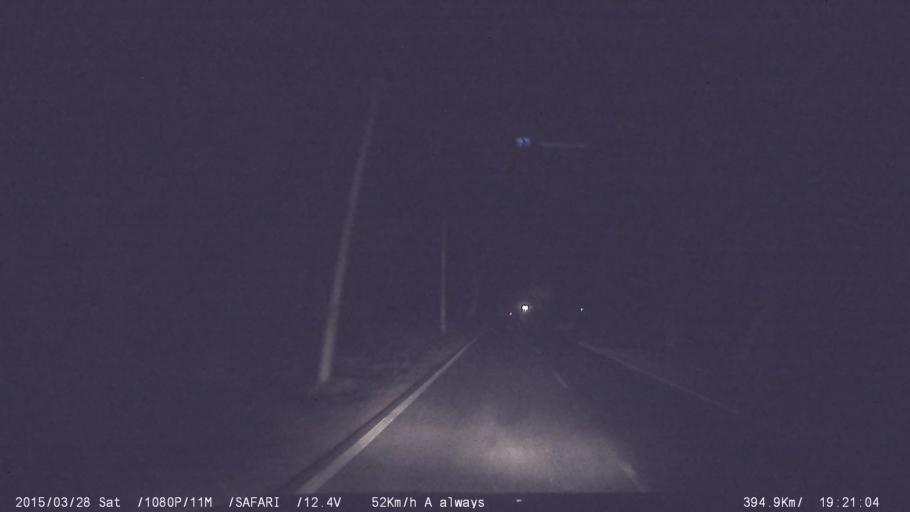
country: IN
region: Karnataka
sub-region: Mandya
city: Shrirangapattana
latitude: 12.4181
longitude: 76.6630
